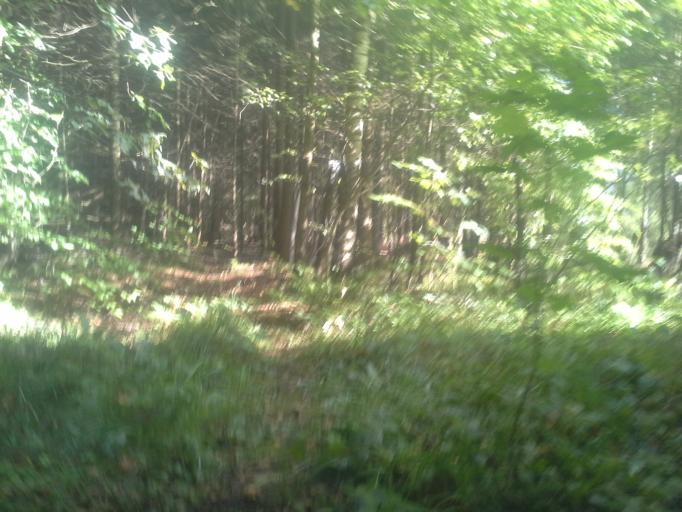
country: RU
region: Moskovskaya
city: Kievskij
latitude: 55.3471
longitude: 36.9577
